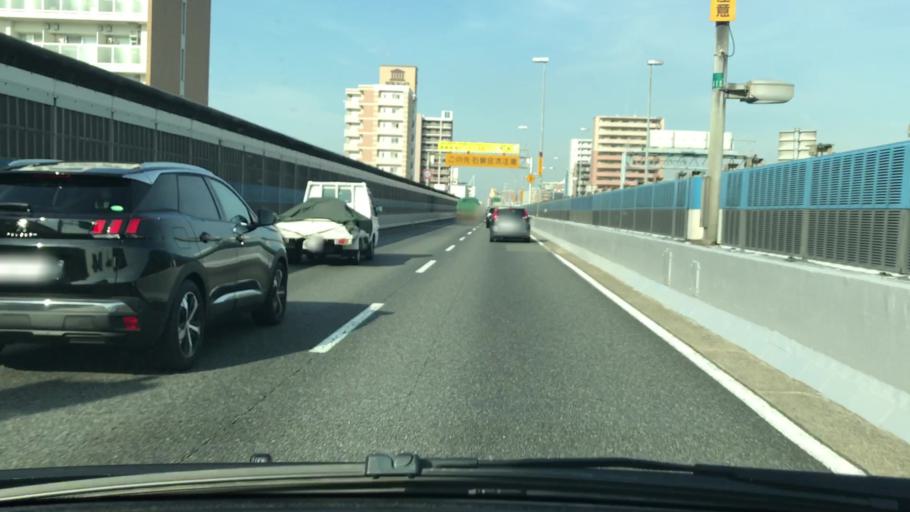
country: JP
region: Hyogo
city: Kobe
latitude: 34.6716
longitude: 135.1749
